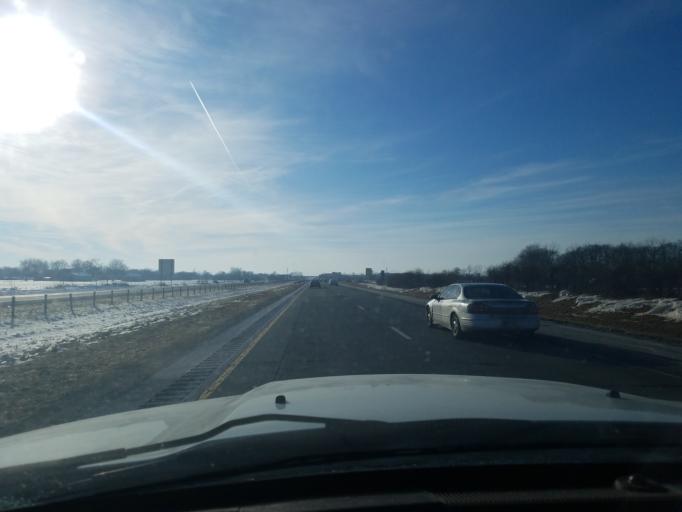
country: US
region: Indiana
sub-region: Madison County
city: Anderson
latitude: 40.0490
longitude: -85.6827
